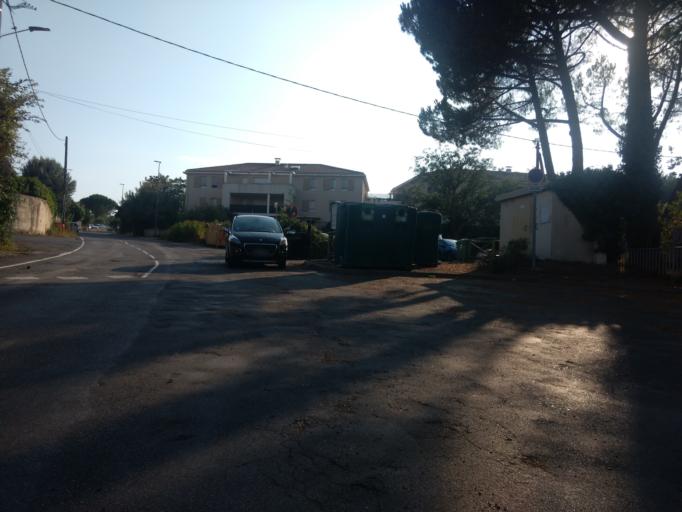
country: FR
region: Provence-Alpes-Cote d'Azur
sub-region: Departement des Alpes-de-Haute-Provence
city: Manosque
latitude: 43.8246
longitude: 5.7765
